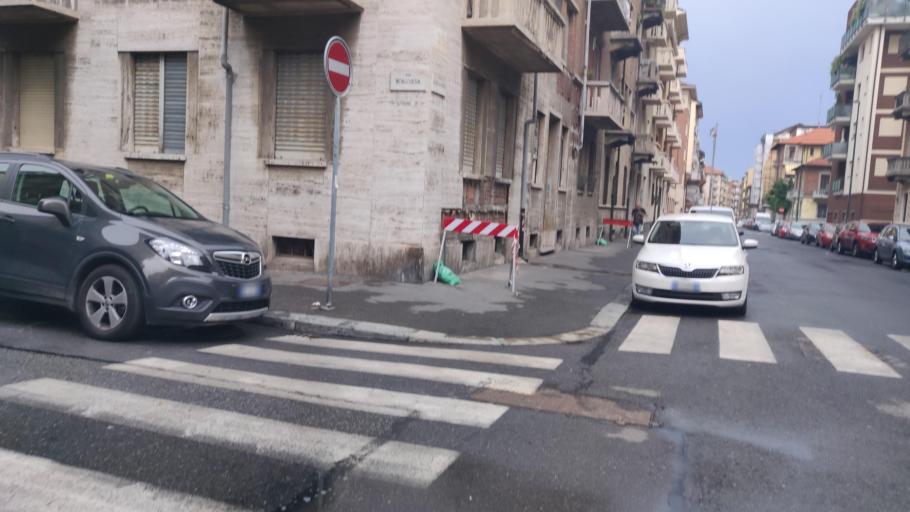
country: IT
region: Piedmont
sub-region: Provincia di Torino
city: Lesna
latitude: 45.0828
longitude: 7.6401
